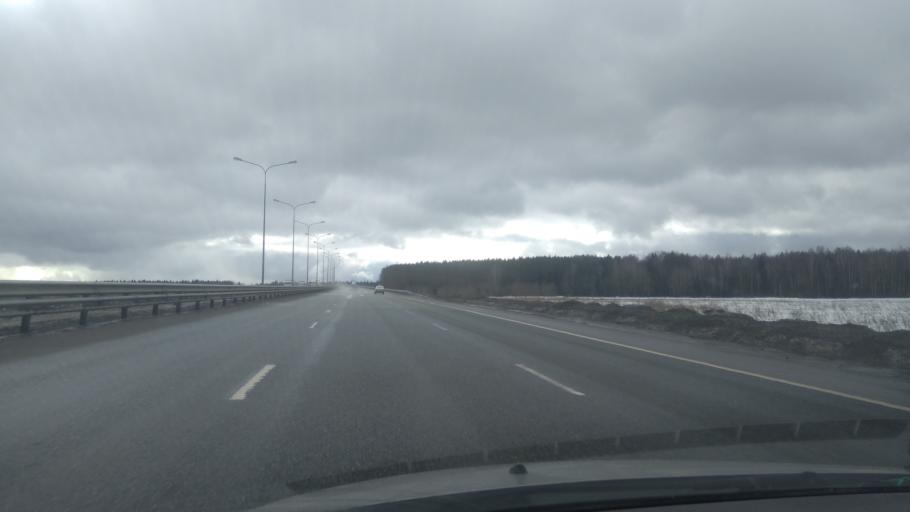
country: RU
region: Perm
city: Bershet'
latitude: 57.7149
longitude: 56.3606
